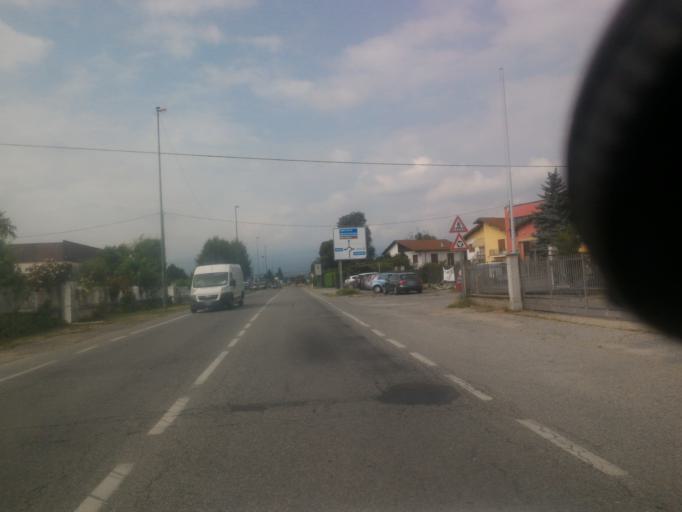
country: IT
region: Piedmont
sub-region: Provincia di Torino
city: Osasco
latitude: 44.8581
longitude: 7.3263
